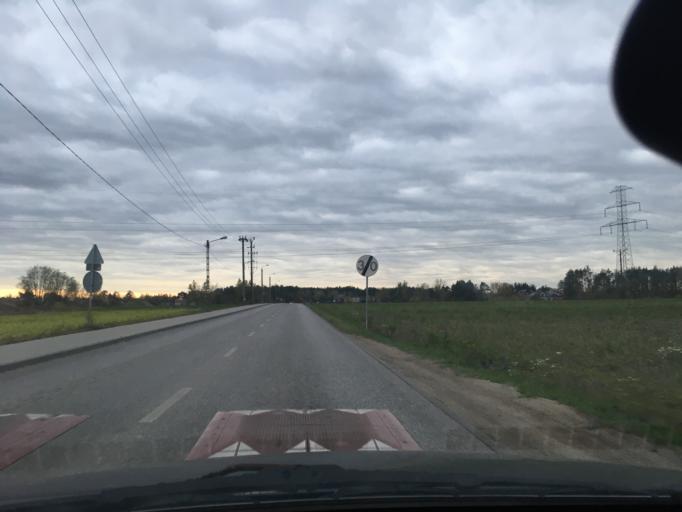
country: PL
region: Masovian Voivodeship
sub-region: Powiat piaseczynski
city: Lesznowola
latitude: 52.0732
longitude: 20.9354
